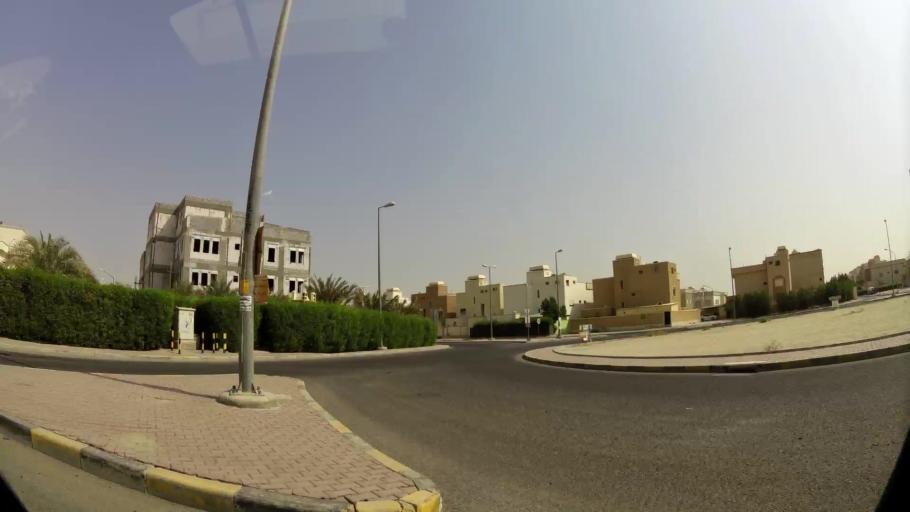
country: KW
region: Muhafazat al Jahra'
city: Al Jahra'
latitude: 29.3235
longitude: 47.7233
